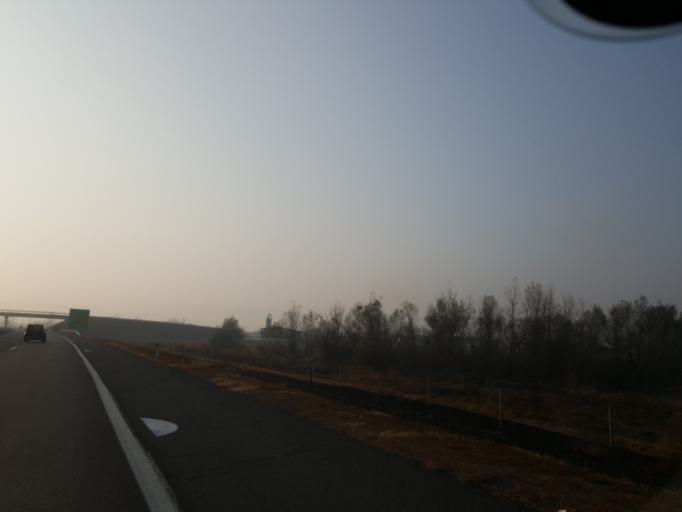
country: RS
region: Central Serbia
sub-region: Jablanicki Okrug
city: Leskovac
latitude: 42.9832
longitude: 22.0295
